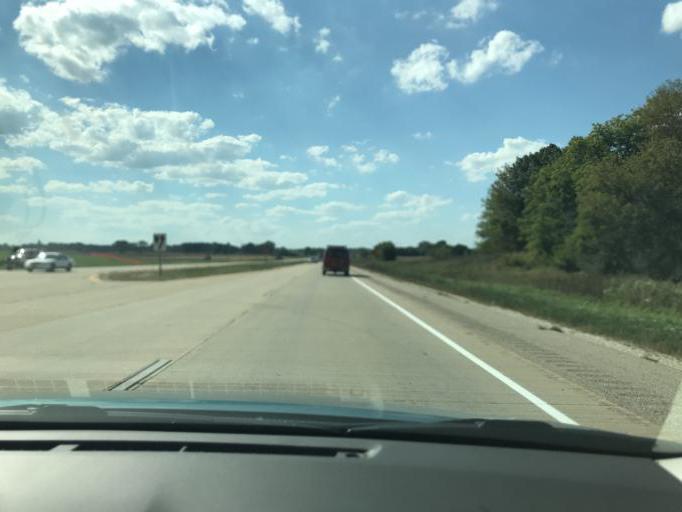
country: US
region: Wisconsin
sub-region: Kenosha County
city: Twin Lakes
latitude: 42.5817
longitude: -88.2320
